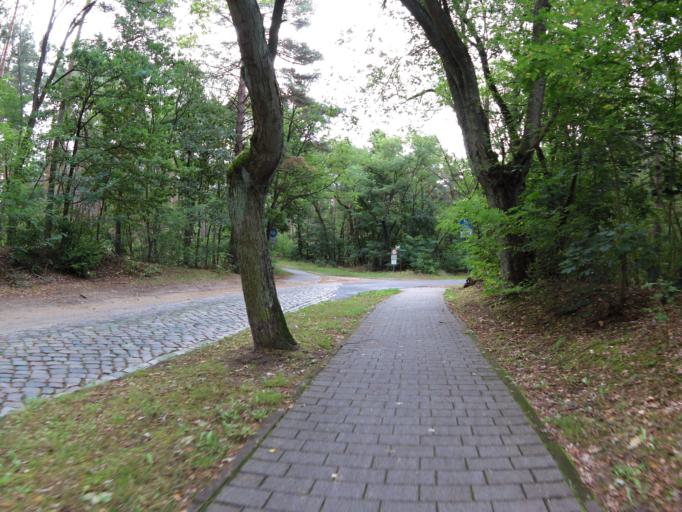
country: DE
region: Brandenburg
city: Storkow
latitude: 52.2589
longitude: 13.9629
